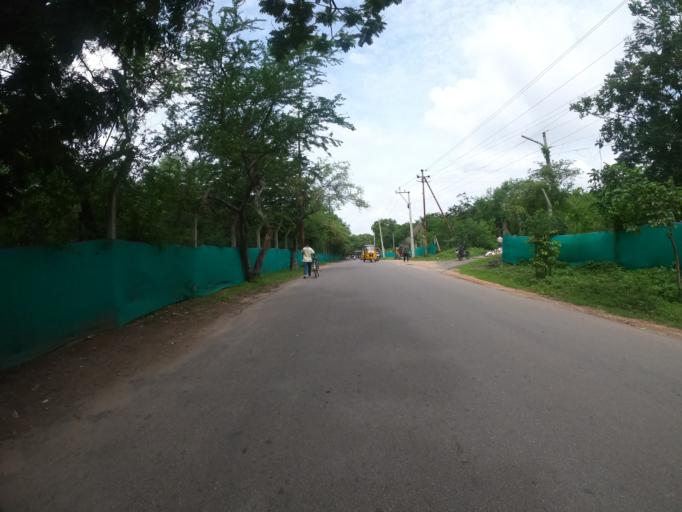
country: IN
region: Telangana
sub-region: Hyderabad
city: Hyderabad
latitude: 17.3915
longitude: 78.4212
